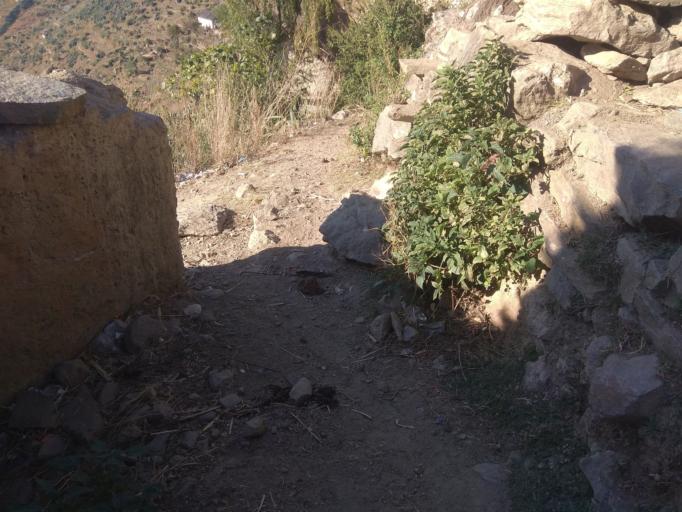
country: NP
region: Mid Western
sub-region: Karnali Zone
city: Jumla
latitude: 29.3130
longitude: 81.7396
